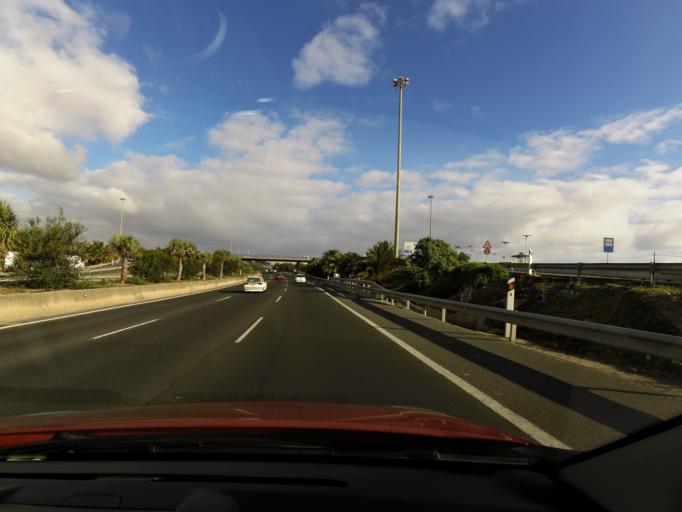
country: ES
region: Canary Islands
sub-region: Provincia de Las Palmas
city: Telde
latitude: 27.9485
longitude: -15.3873
